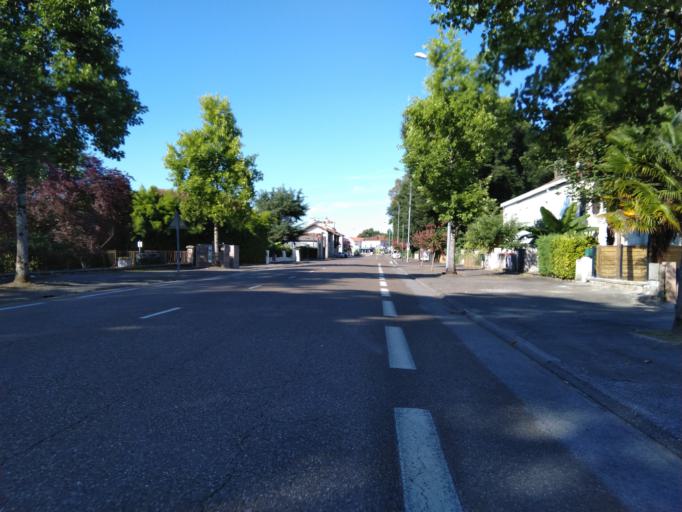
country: FR
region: Aquitaine
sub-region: Departement des Landes
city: Saint-Paul-les-Dax
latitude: 43.7249
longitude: -1.0487
